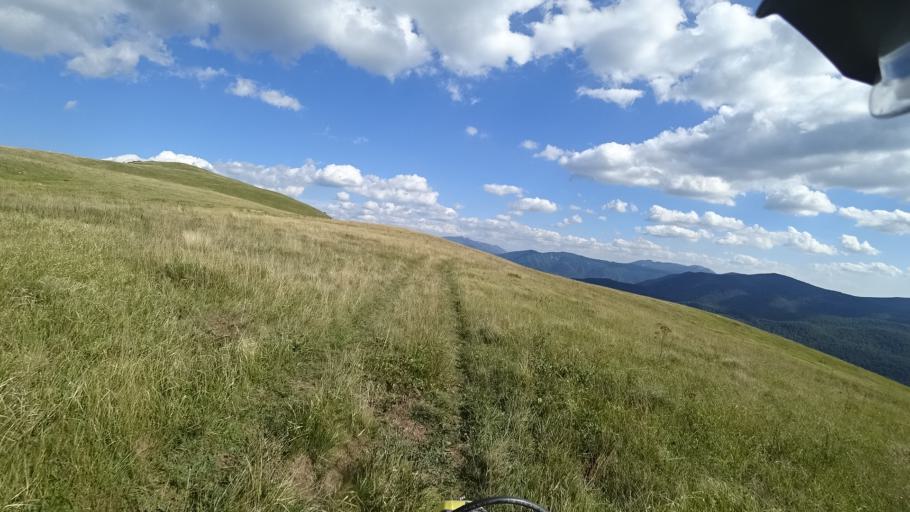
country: HR
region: Zadarska
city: Gracac
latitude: 44.3730
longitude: 16.0549
